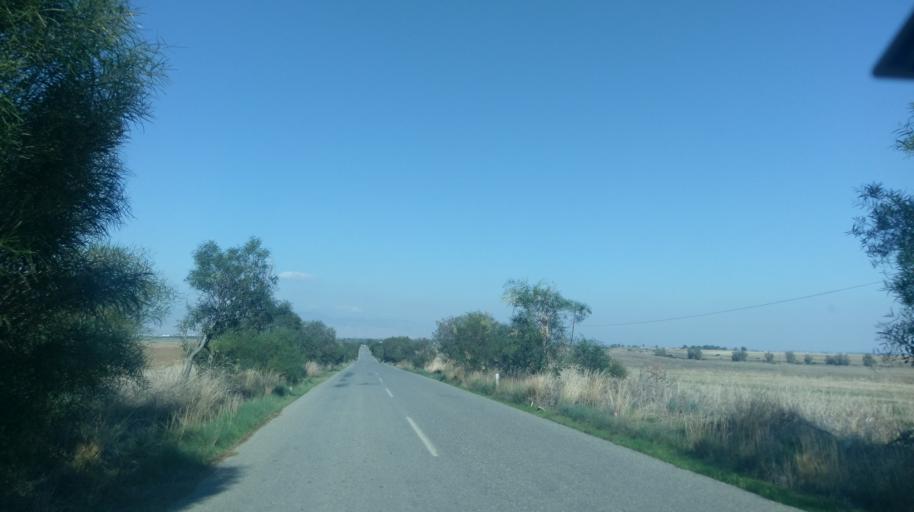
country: CY
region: Larnaka
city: Athienou
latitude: 35.1065
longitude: 33.4968
